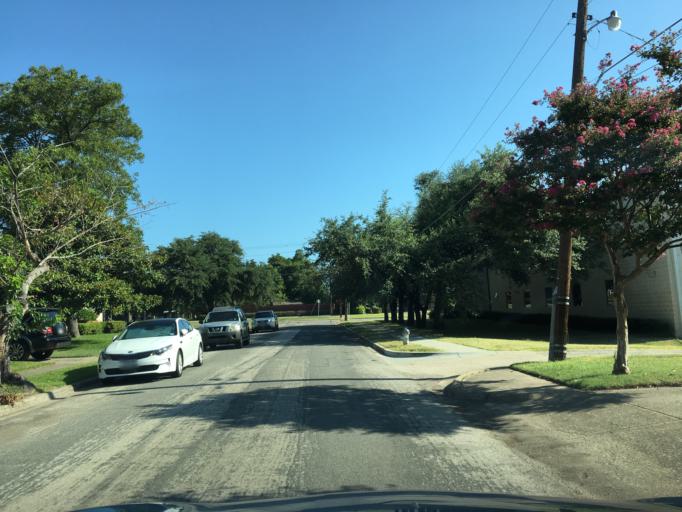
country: US
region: Texas
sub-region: Dallas County
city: Garland
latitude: 32.8632
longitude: -96.7073
